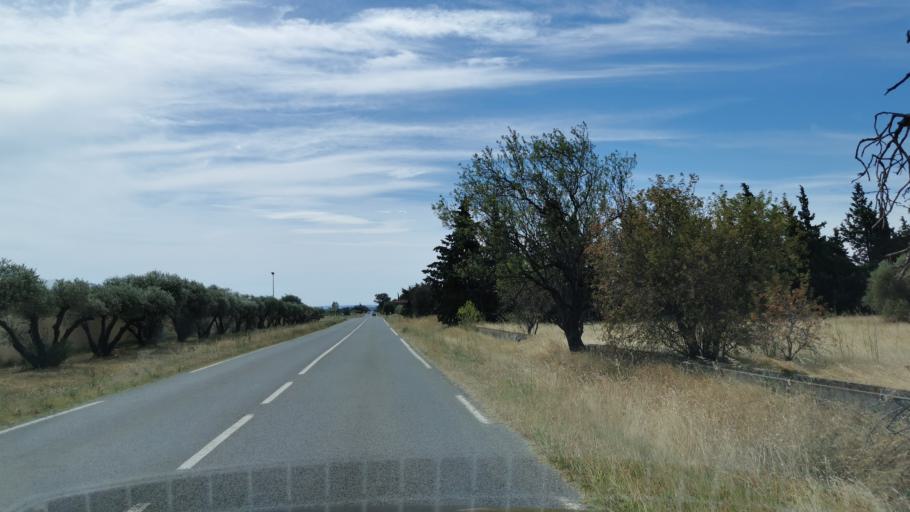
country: FR
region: Languedoc-Roussillon
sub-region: Departement de l'Aude
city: Ginestas
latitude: 43.2768
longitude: 2.8845
